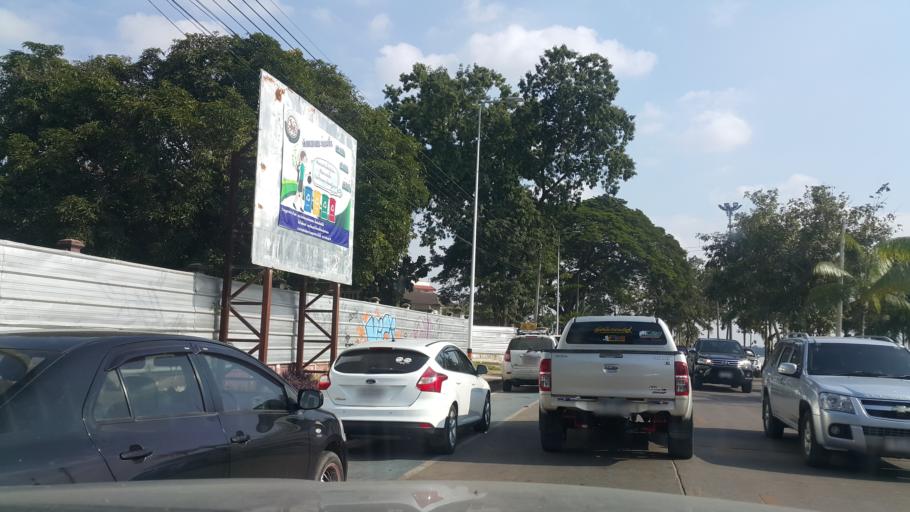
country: TH
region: Phayao
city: Phayao
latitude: 19.1646
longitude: 99.8967
